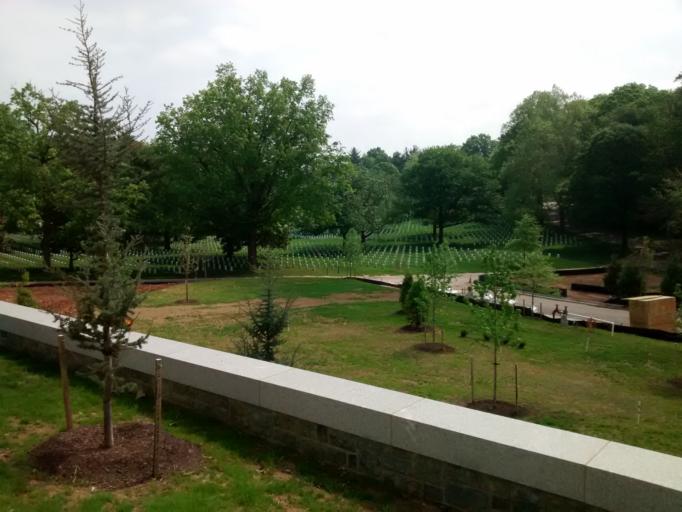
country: US
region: Virginia
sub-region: Arlington County
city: Arlington
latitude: 38.8842
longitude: -77.0741
